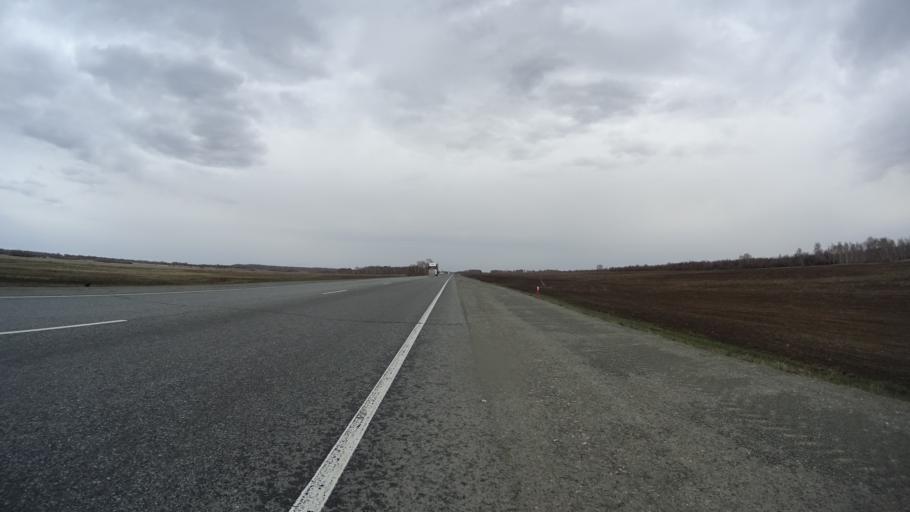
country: RU
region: Chelyabinsk
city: Krasnogorskiy
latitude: 54.6682
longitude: 61.2517
